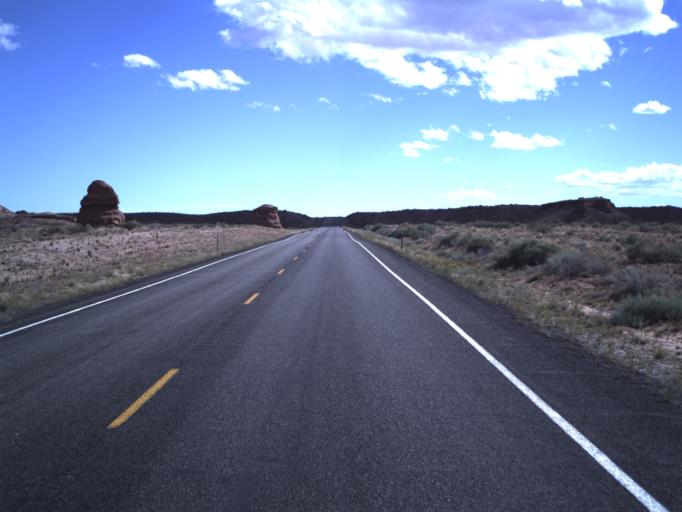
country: US
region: Utah
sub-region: Emery County
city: Ferron
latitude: 38.3590
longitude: -110.6984
